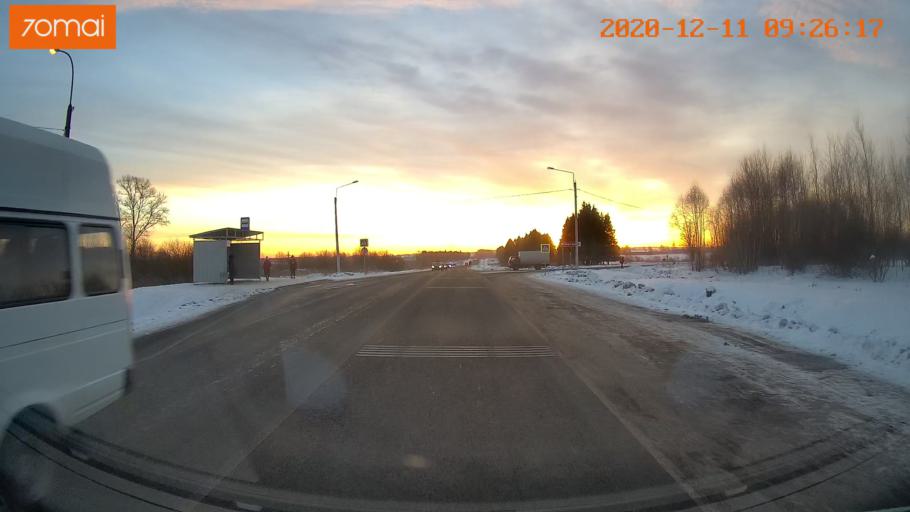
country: RU
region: Vologda
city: Vologda
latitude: 59.1708
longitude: 39.9866
